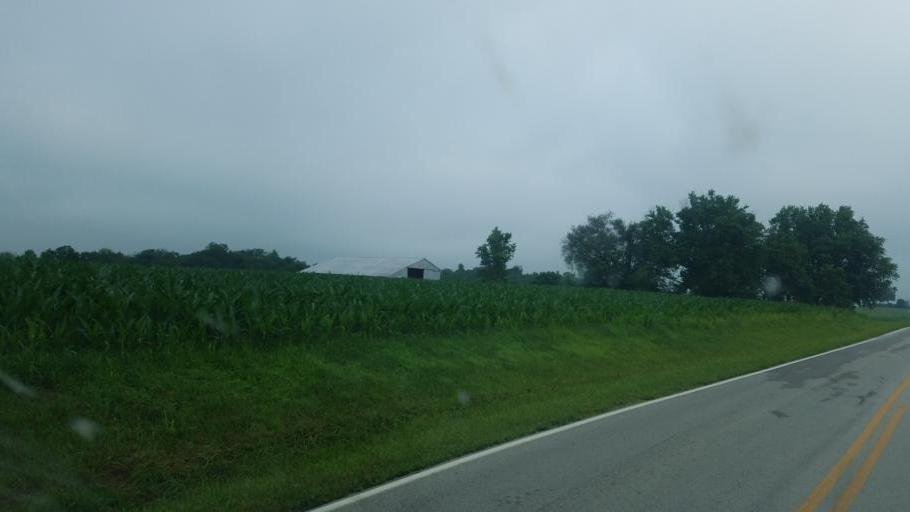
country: US
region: Ohio
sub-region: Highland County
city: Hillsboro
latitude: 39.2390
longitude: -83.5855
